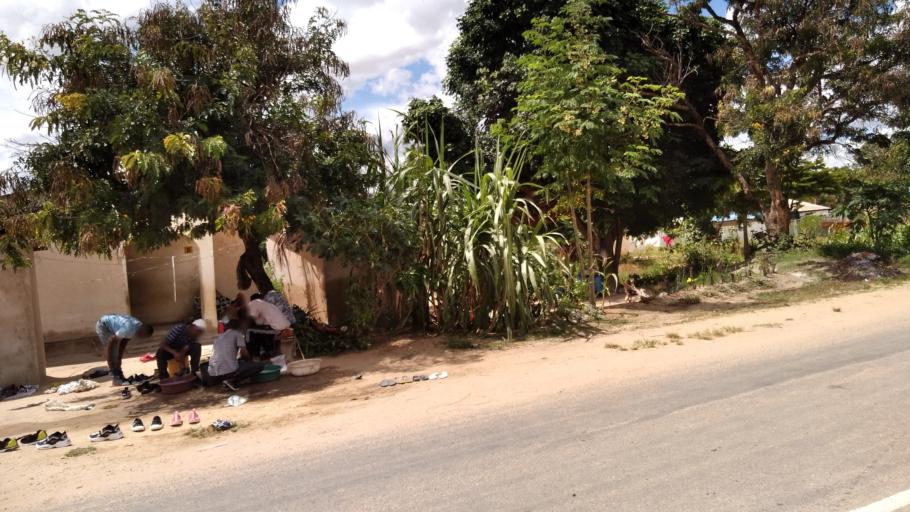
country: TZ
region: Dodoma
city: Dodoma
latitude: -6.1600
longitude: 35.7371
